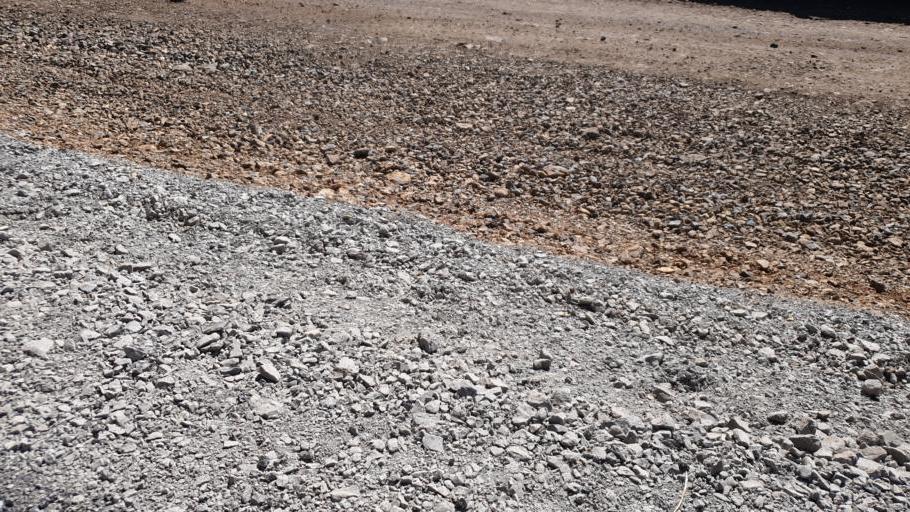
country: ET
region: Oromiya
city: Fiche
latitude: 9.6509
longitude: 38.9901
